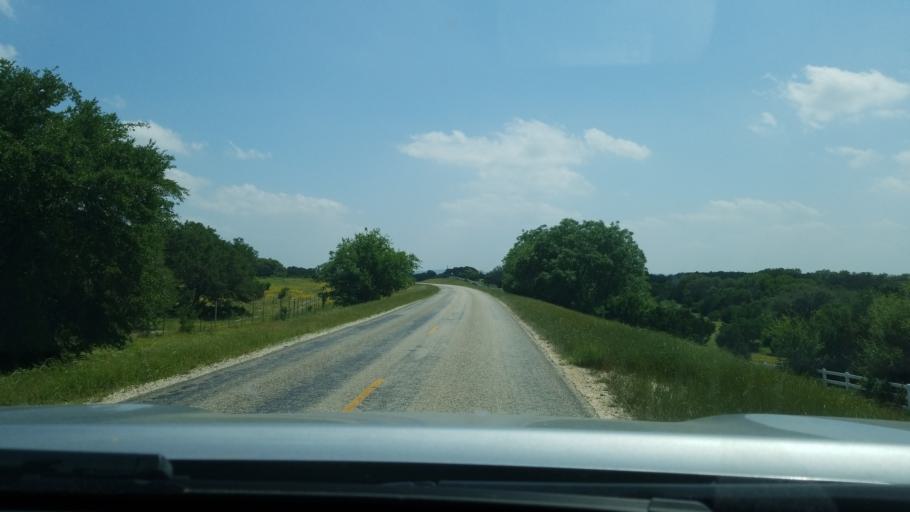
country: US
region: Texas
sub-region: Bexar County
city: Fair Oaks Ranch
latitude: 29.9273
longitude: -98.5710
